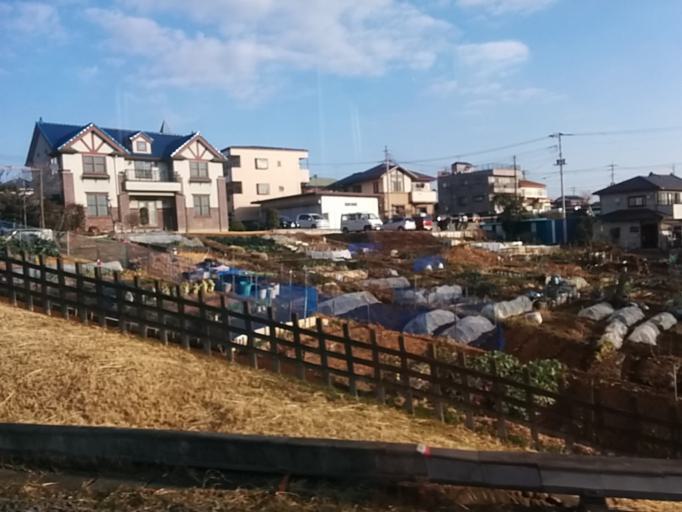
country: JP
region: Saitama
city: Shiki
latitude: 35.8350
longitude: 139.5556
